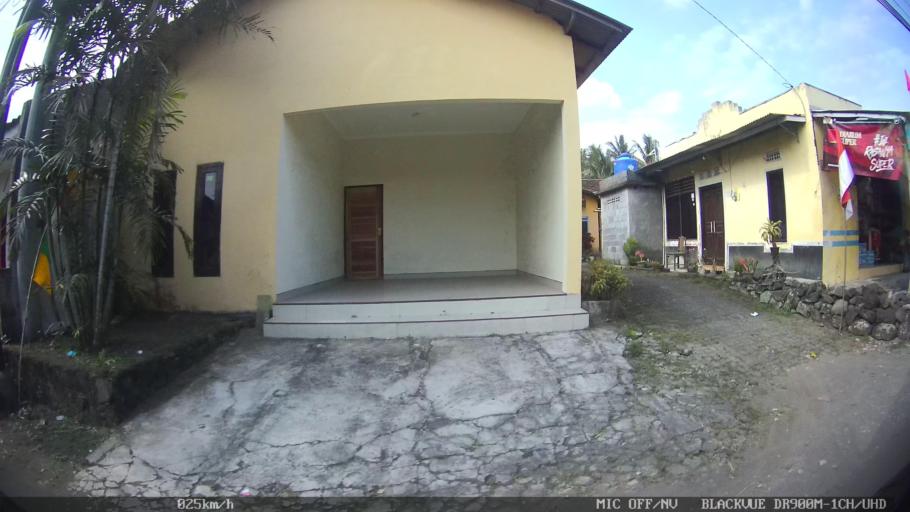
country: ID
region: Daerah Istimewa Yogyakarta
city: Depok
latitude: -7.7288
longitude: 110.4121
